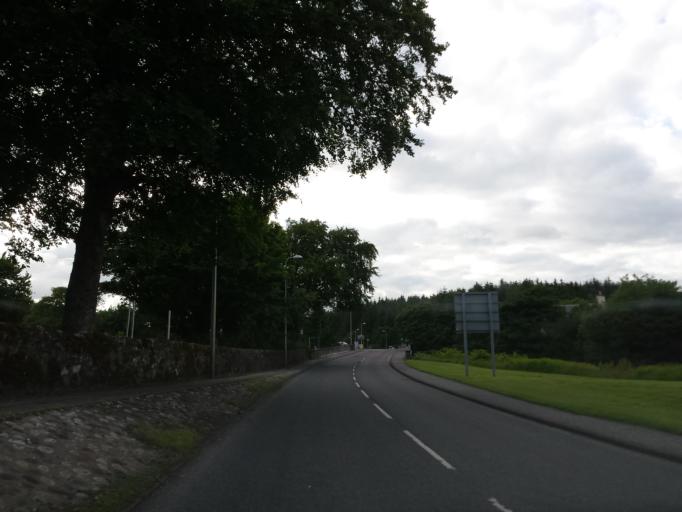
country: GB
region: Scotland
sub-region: Highland
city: Portree
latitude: 57.2419
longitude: -5.9114
